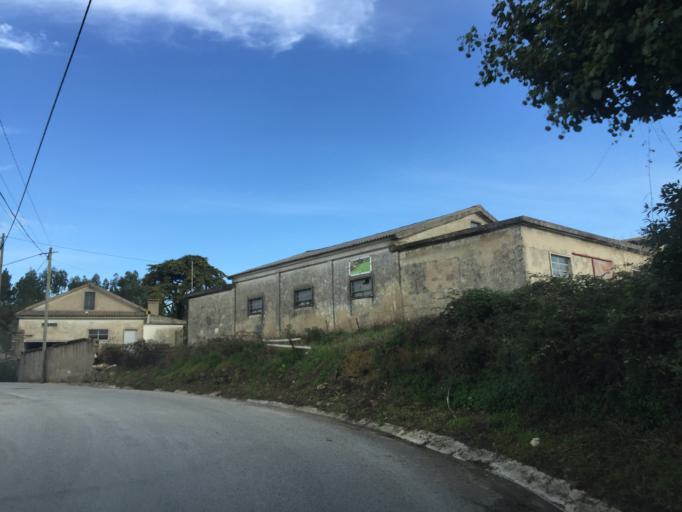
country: PT
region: Lisbon
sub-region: Odivelas
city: Canecas
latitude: 38.8183
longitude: -9.2474
